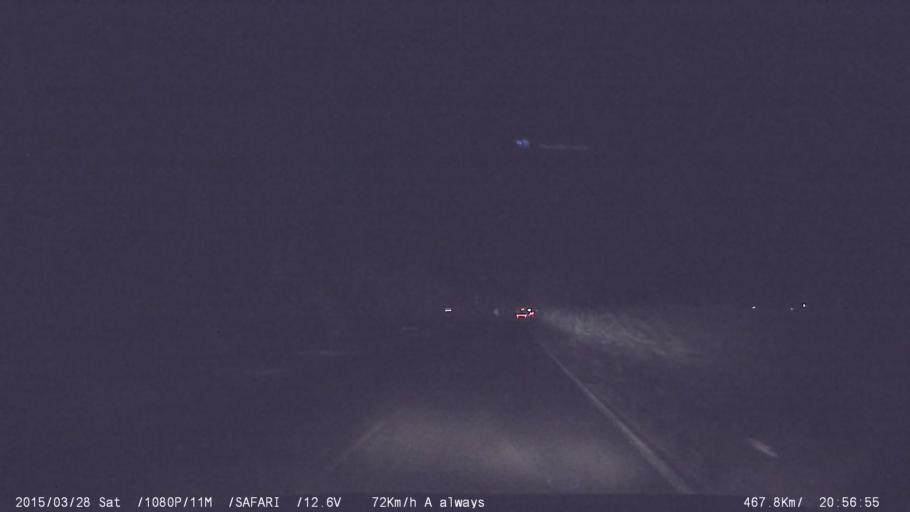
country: IN
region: Karnataka
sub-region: Ramanagara
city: Ramanagaram
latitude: 12.6944
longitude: 77.2459
